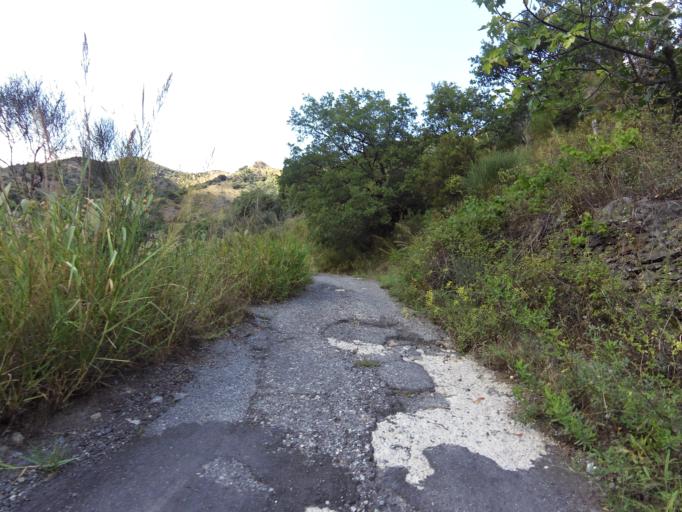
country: IT
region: Calabria
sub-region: Provincia di Reggio Calabria
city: Bivongi
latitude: 38.4914
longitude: 16.4555
